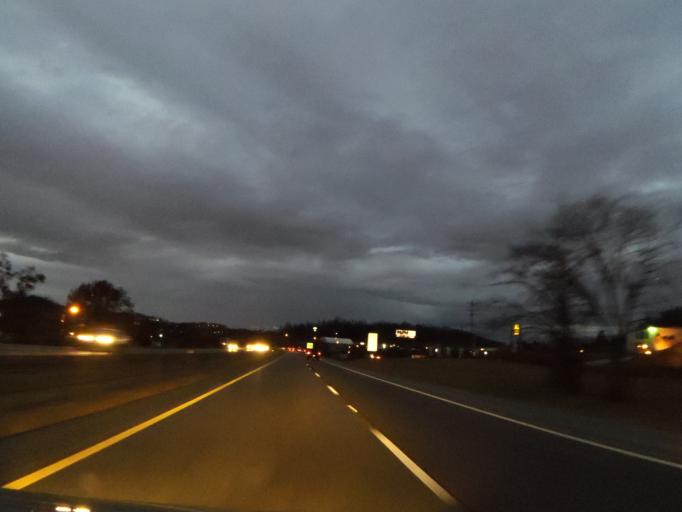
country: US
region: Tennessee
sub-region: Sullivan County
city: Colonial Heights
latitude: 36.4433
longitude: -82.5221
